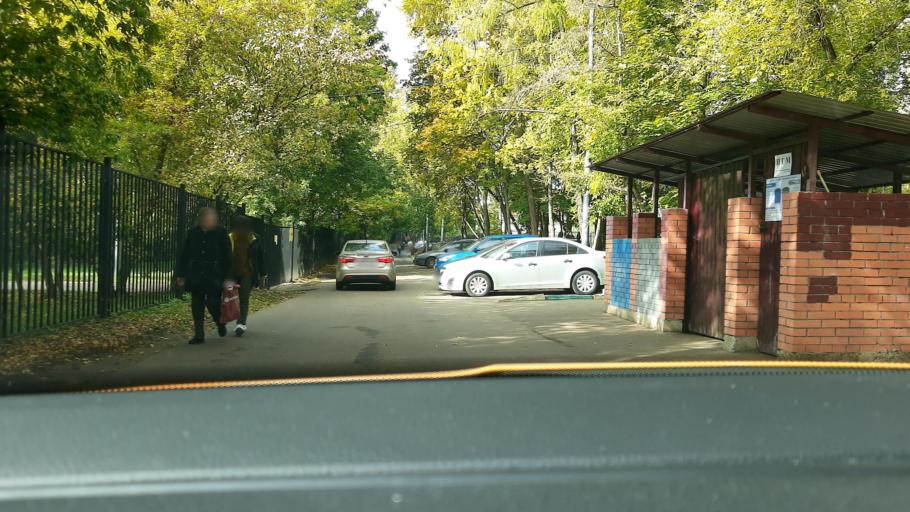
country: RU
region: Moscow
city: Novokuz'minki
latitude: 55.6978
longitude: 37.7726
